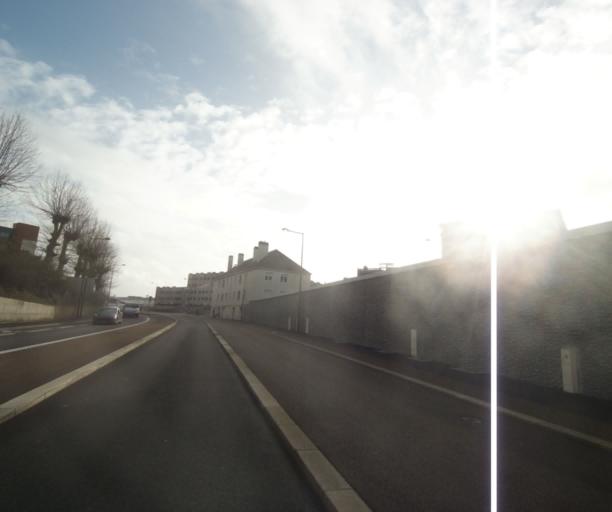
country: FR
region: Pays de la Loire
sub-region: Departement de la Sarthe
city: Le Mans
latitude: 47.9978
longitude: 0.1890
